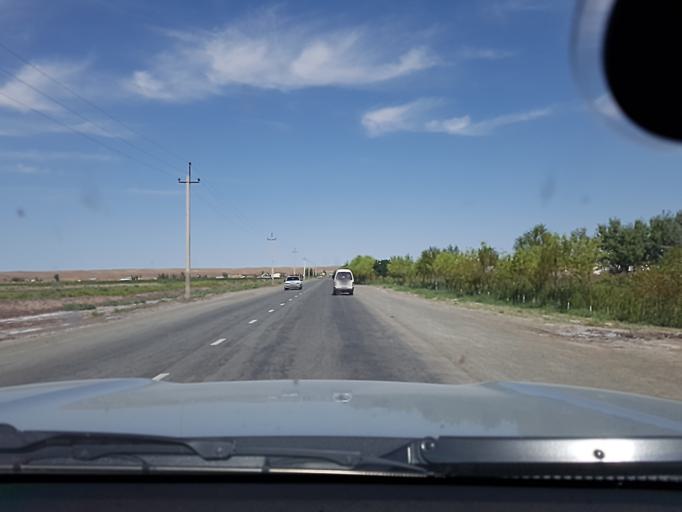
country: UZ
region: Karakalpakstan
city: Mang'it Shahri
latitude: 42.2377
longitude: 60.1418
